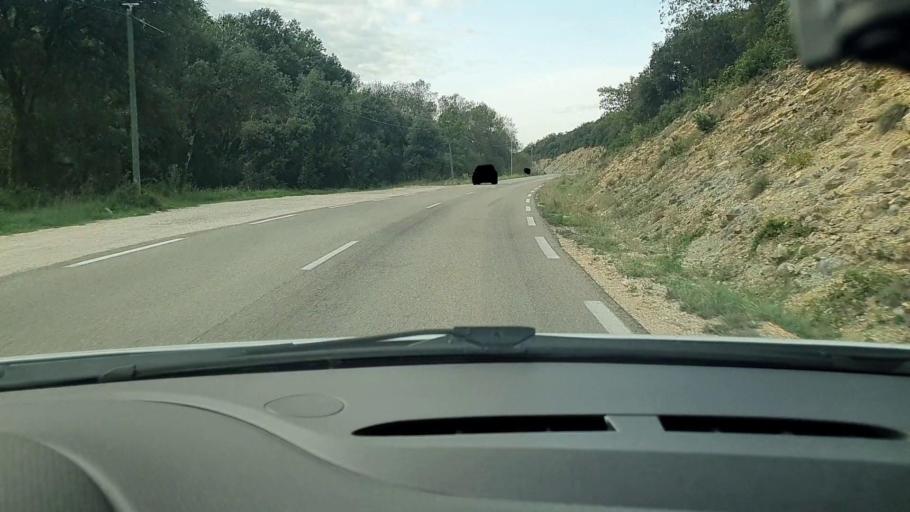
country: FR
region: Languedoc-Roussillon
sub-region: Departement du Gard
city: Mons
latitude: 44.0992
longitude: 4.2236
